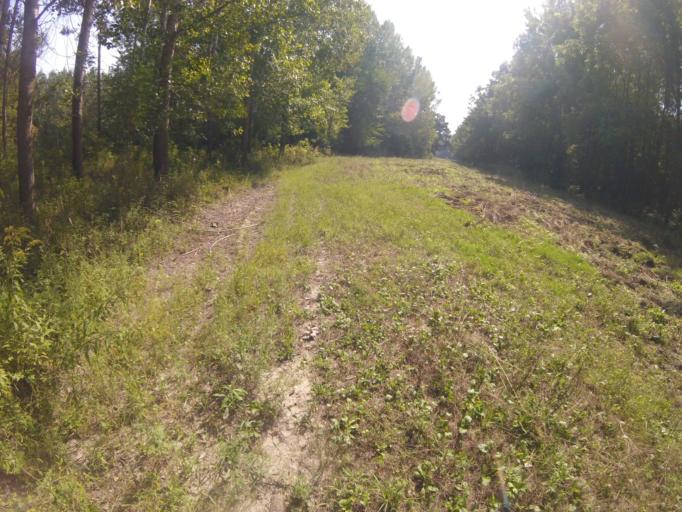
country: HU
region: Bacs-Kiskun
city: Baja
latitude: 46.2244
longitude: 18.8812
